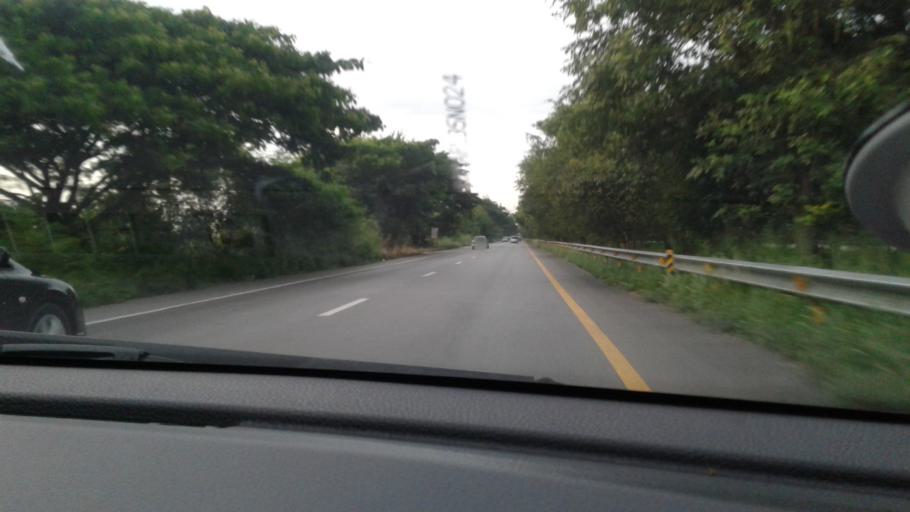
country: TH
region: Prachuap Khiri Khan
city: Hua Hin
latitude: 12.4981
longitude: 99.8876
